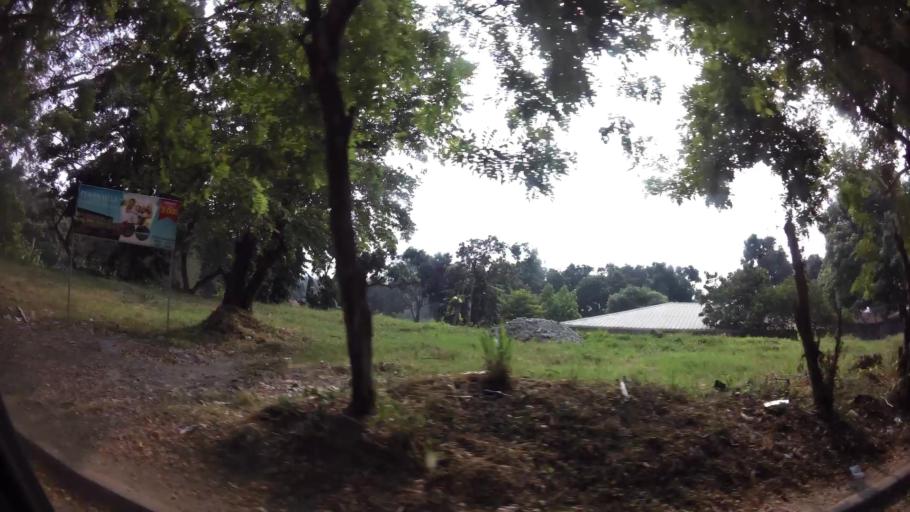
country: HN
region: Cortes
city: El Zapotal del Norte
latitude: 15.5175
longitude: -88.0496
